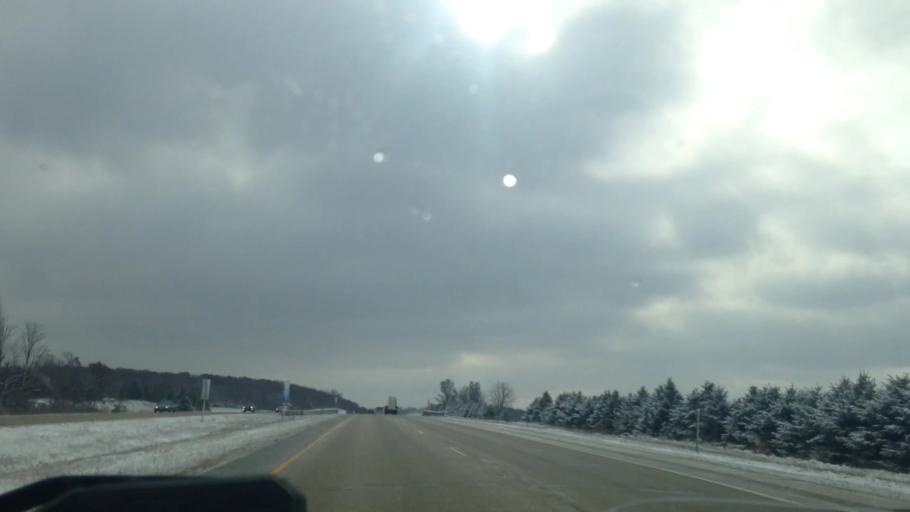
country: US
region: Wisconsin
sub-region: Washington County
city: Slinger
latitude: 43.3710
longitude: -88.2992
